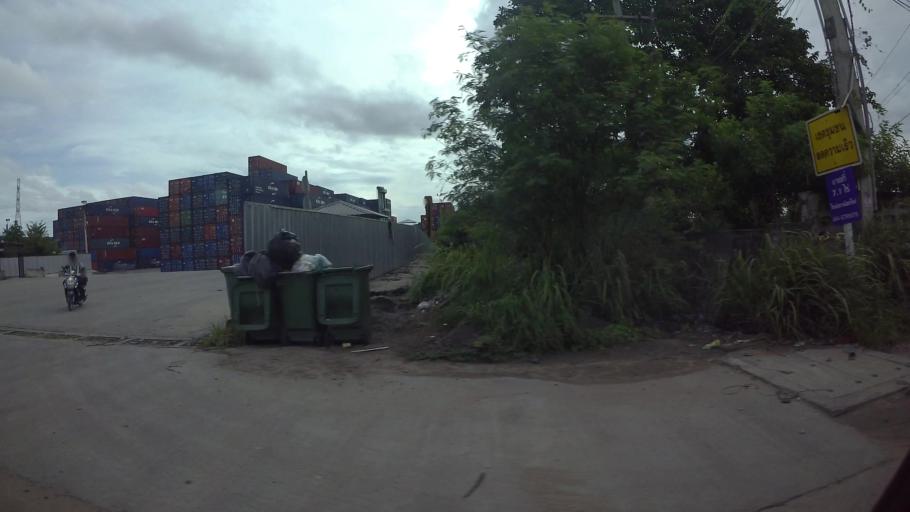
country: TH
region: Chon Buri
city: Ban Talat Bueng
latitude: 13.1181
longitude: 100.9732
